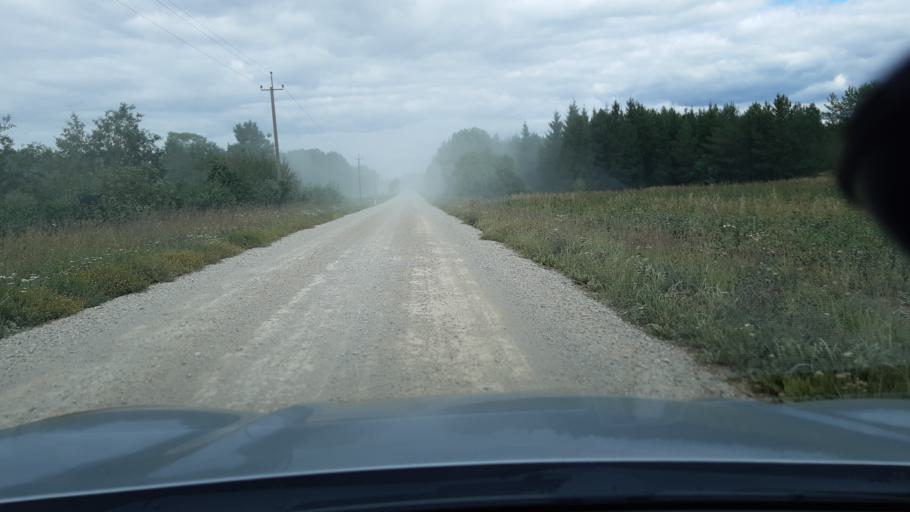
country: EE
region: Raplamaa
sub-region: Maerjamaa vald
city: Marjamaa
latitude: 58.9392
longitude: 24.3109
